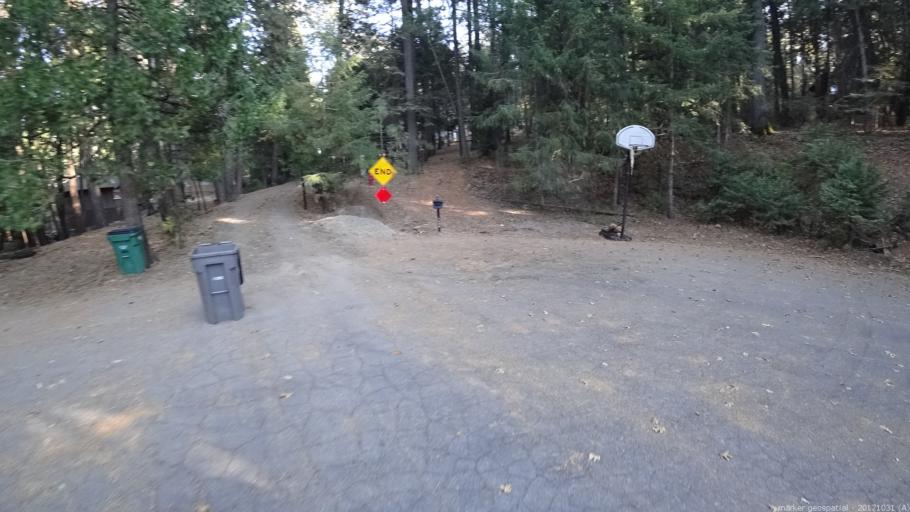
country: US
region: California
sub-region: Shasta County
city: Shingletown
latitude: 40.4993
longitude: -121.8997
